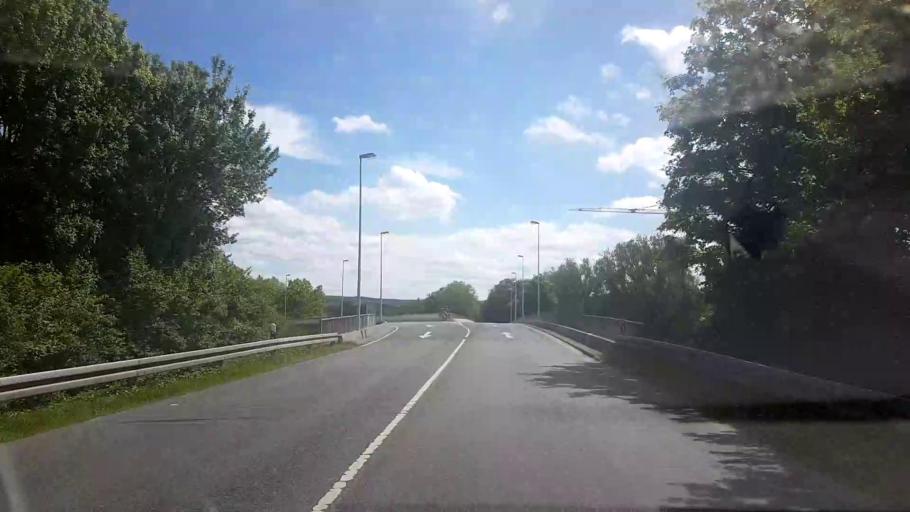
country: DE
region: Bavaria
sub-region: Upper Franconia
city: Coburg
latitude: 50.2425
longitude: 10.9707
